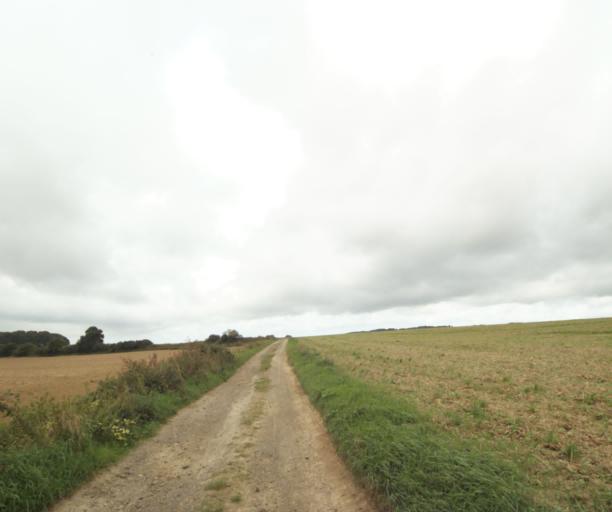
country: FR
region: Nord-Pas-de-Calais
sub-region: Departement du Pas-de-Calais
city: Etaples
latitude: 50.5310
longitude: 1.6738
